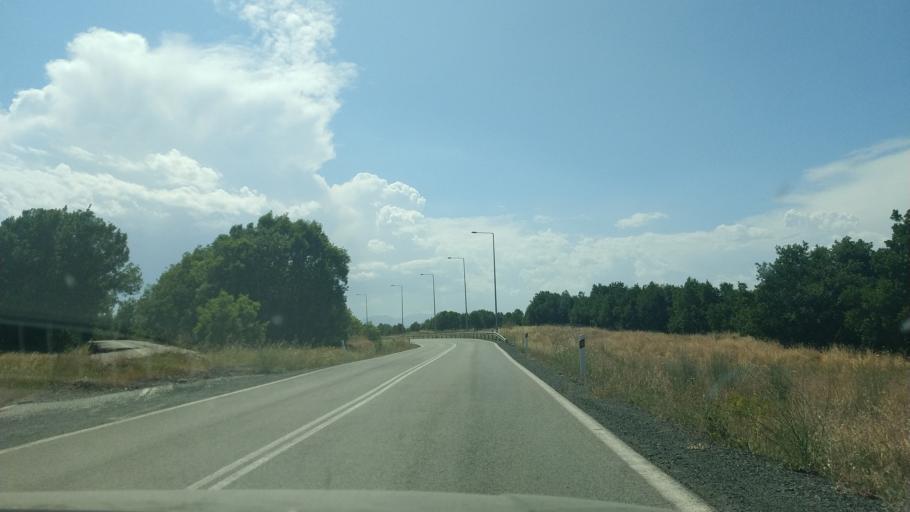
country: GR
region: West Macedonia
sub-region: Nomos Grevenon
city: Grevena
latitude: 40.0674
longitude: 21.4466
